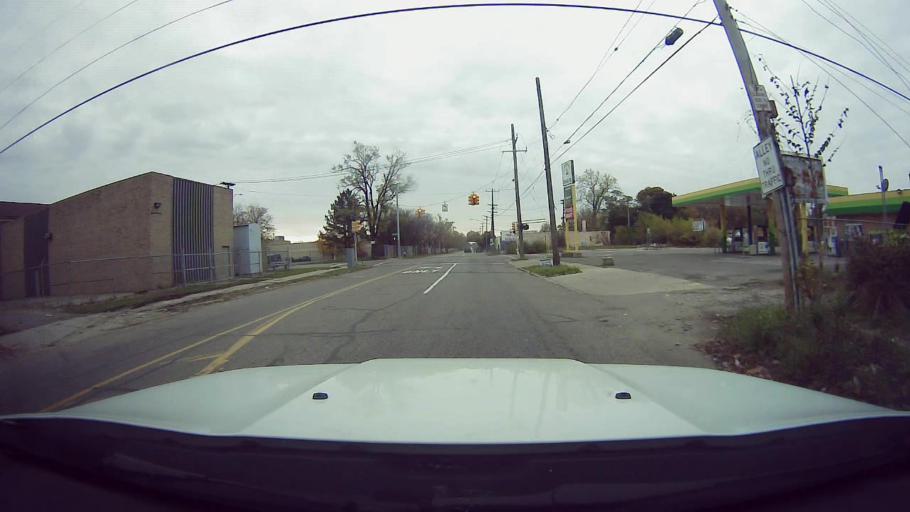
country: US
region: Michigan
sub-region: Wayne County
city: Dearborn
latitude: 42.3660
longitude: -83.1876
